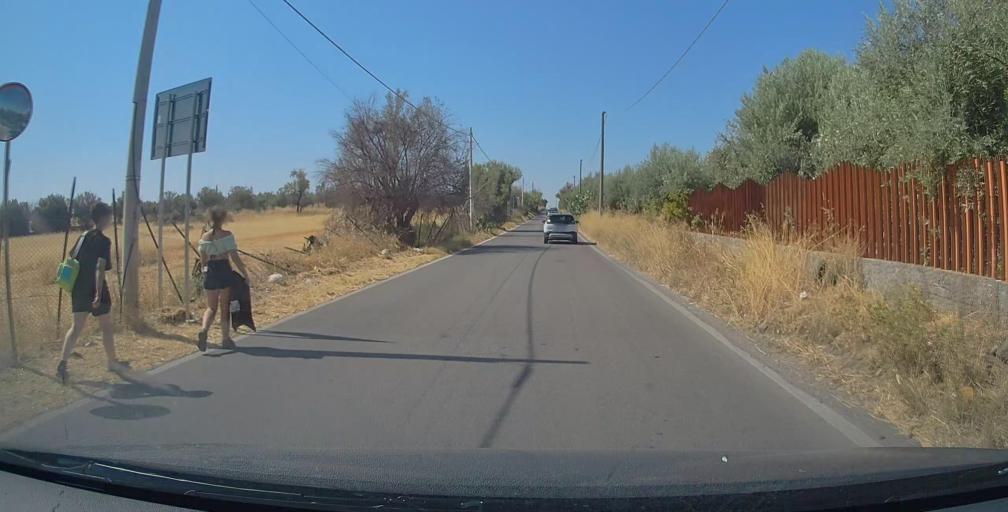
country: IT
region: Sicily
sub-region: Catania
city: Palazzolo
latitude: 37.5450
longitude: 14.9303
